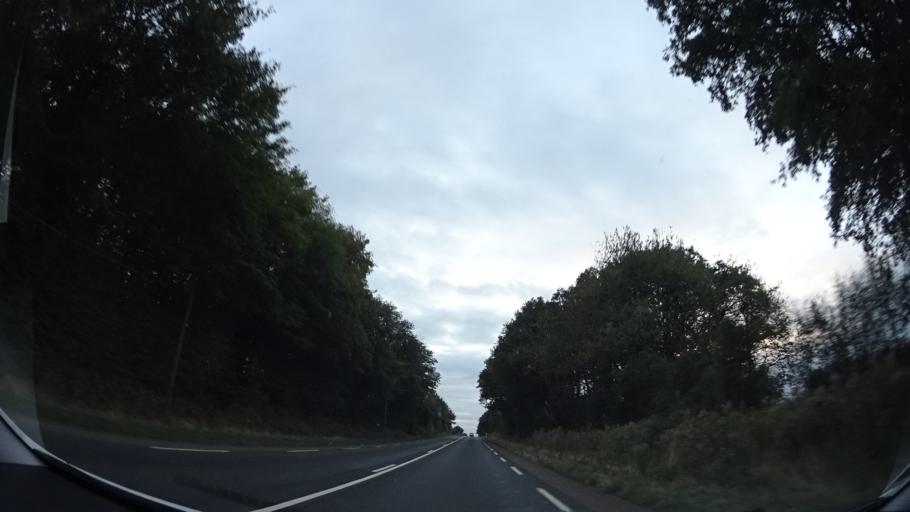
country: FR
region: Pays de la Loire
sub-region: Departement de la Mayenne
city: Sainte-Suzanne
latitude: 48.0322
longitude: -0.3260
